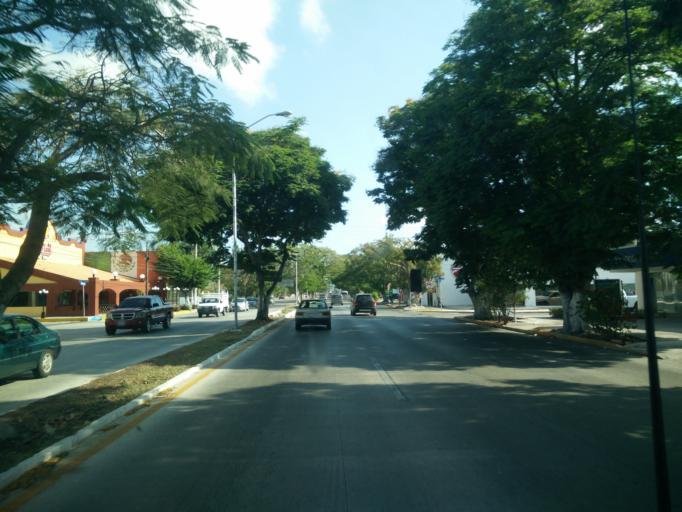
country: MX
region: Yucatan
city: Merida
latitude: 21.0043
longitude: -89.6148
